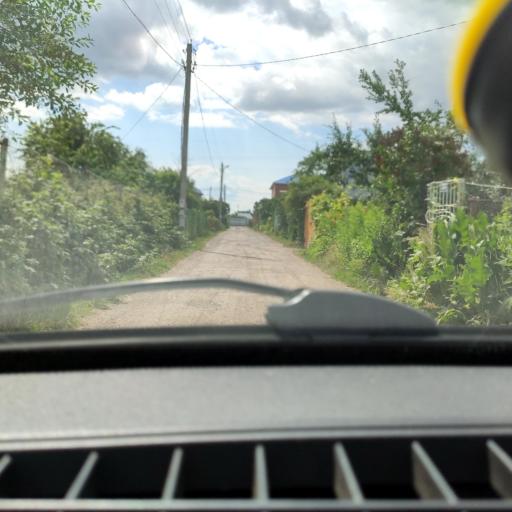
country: RU
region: Samara
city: Podstepki
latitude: 53.5983
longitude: 49.2245
